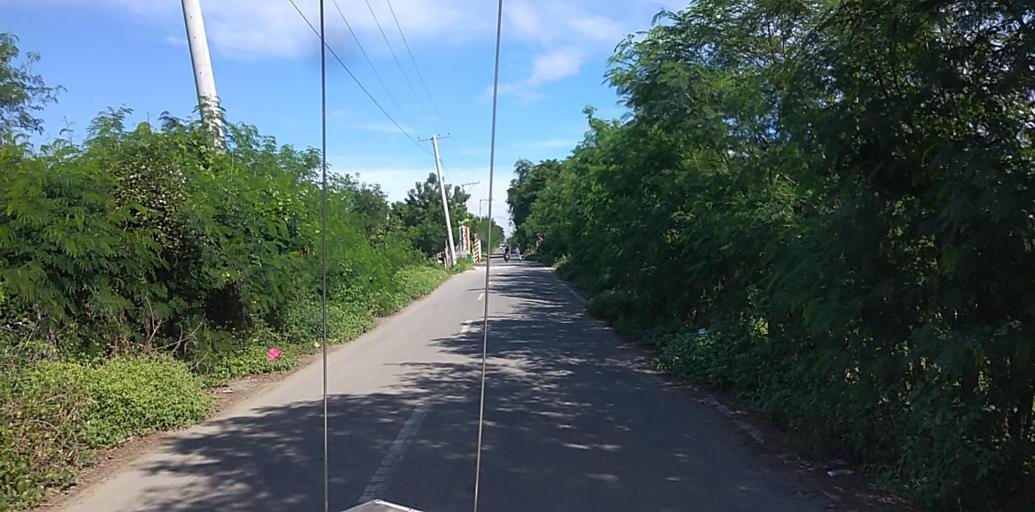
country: PH
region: Central Luzon
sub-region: Province of Pampanga
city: Candaba
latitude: 15.0717
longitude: 120.8063
